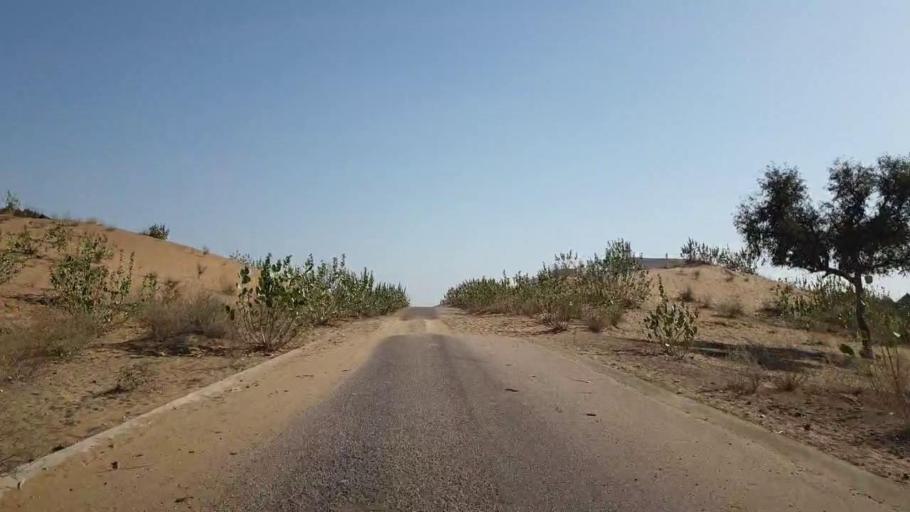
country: PK
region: Sindh
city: Umarkot
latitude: 25.1044
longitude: 70.0382
